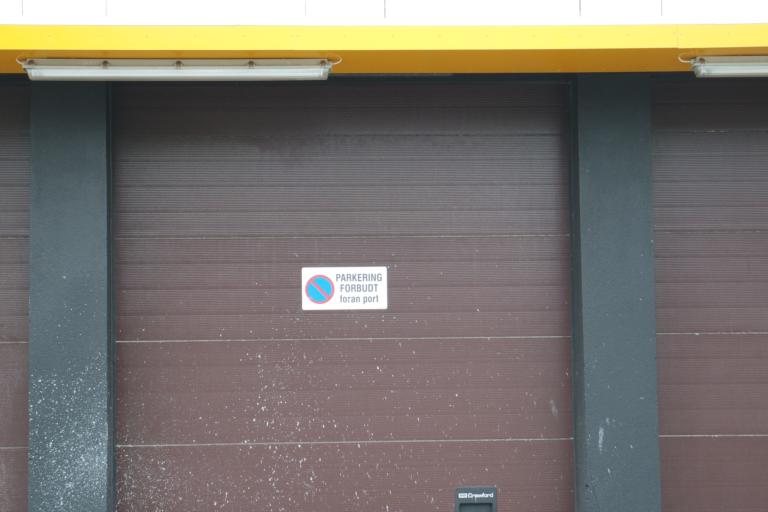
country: NO
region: Nordland
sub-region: Vagan
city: Svolvaer
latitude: 68.2306
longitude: 14.5632
